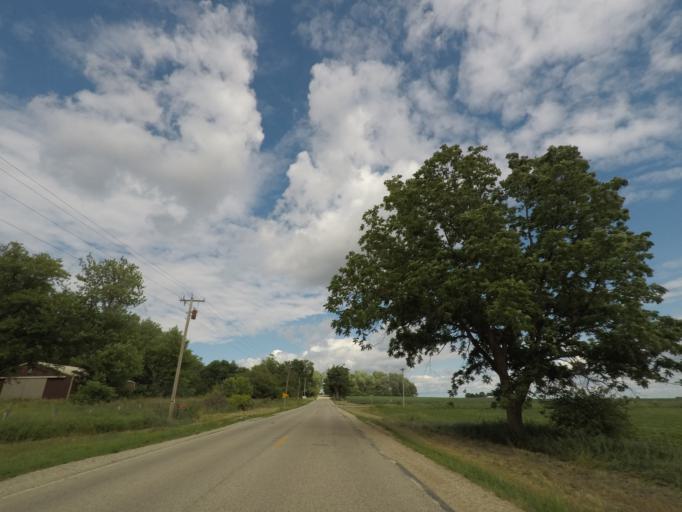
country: US
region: Wisconsin
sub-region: Rock County
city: Orfordville
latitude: 42.7126
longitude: -89.2109
